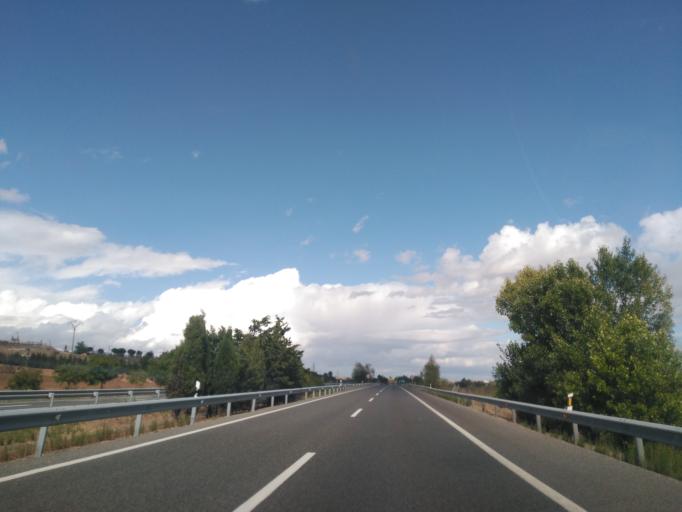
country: ES
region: Castille and Leon
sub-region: Provincia de Burgos
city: Villaldemiro
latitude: 42.2388
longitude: -3.9770
